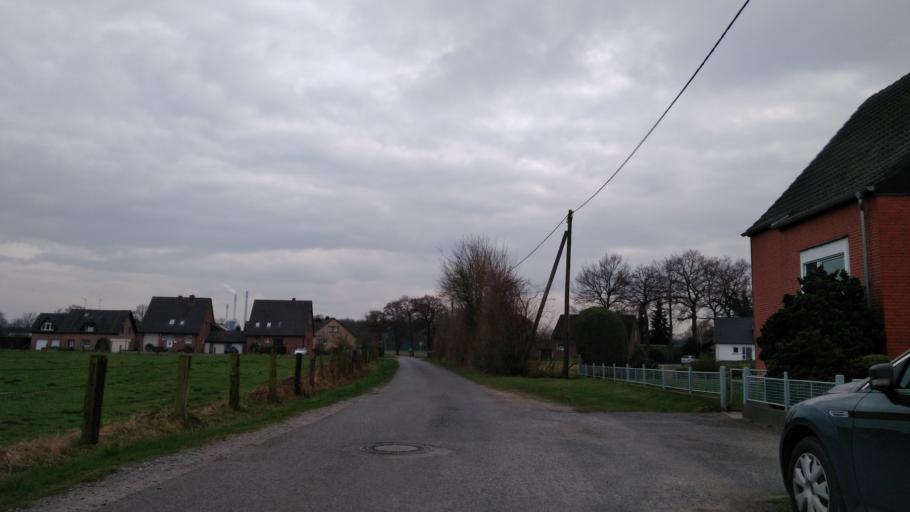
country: DE
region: North Rhine-Westphalia
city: Dorsten
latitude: 51.6411
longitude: 6.9828
